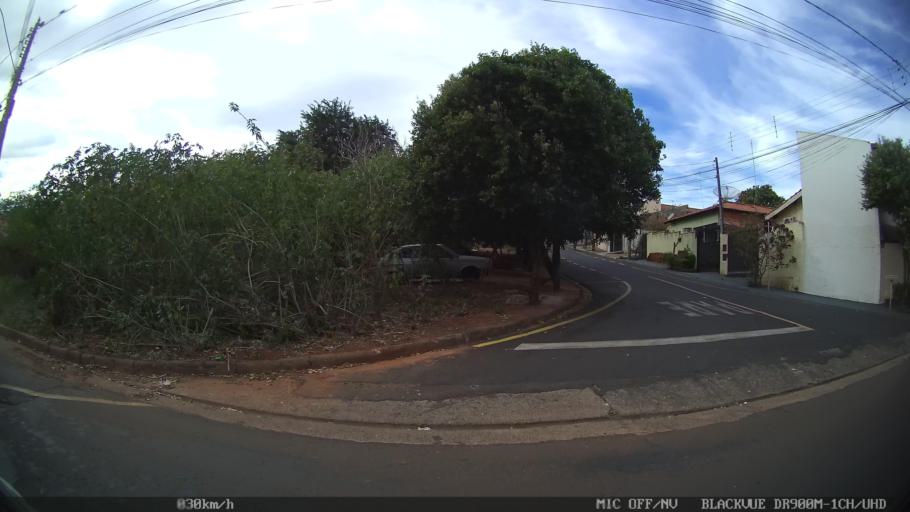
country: BR
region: Sao Paulo
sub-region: Catanduva
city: Catanduva
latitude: -21.1389
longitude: -48.9889
